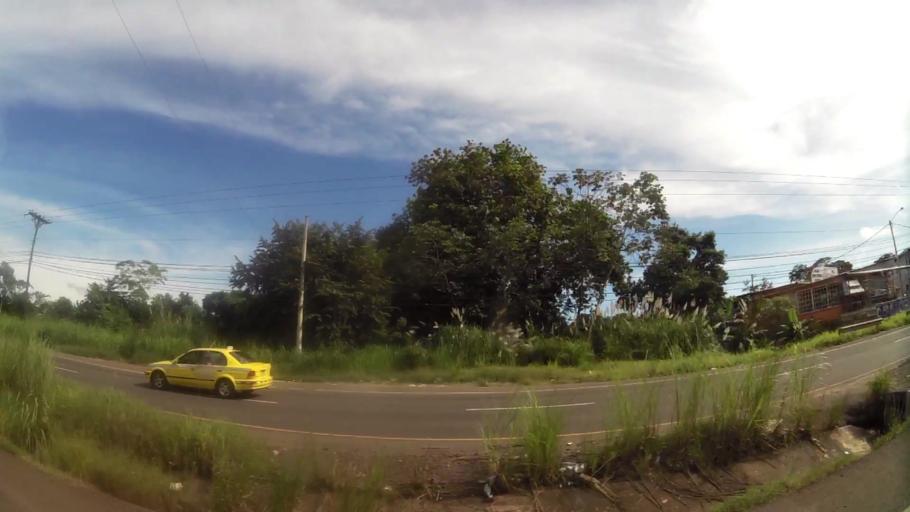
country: PA
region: Panama
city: La Chorrera
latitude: 8.8955
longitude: -79.7596
